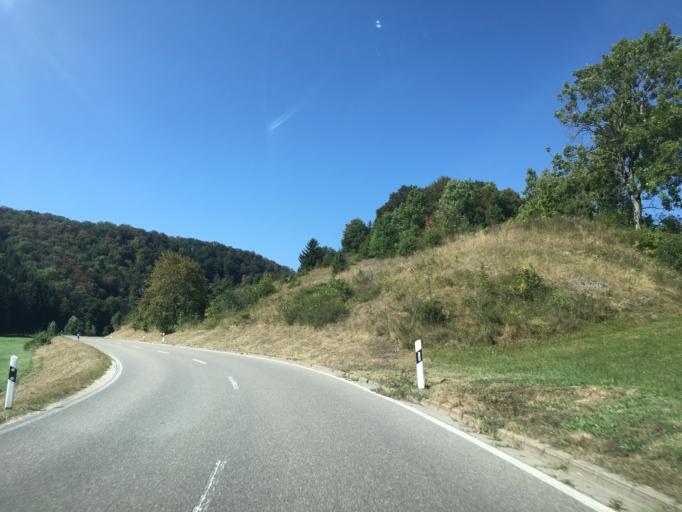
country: DE
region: Baden-Wuerttemberg
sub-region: Tuebingen Region
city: Hayingen
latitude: 48.3353
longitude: 9.4985
